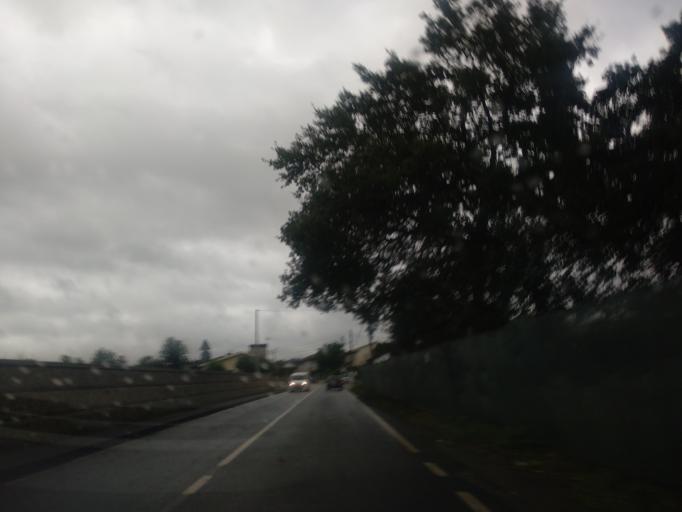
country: PT
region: Braga
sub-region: Guimaraes
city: Ponte
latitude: 41.4796
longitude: -8.3292
